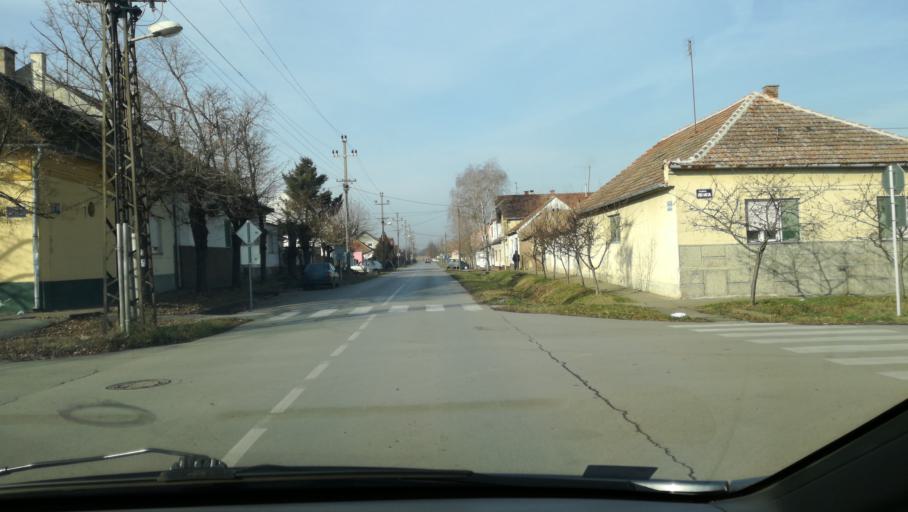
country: RS
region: Autonomna Pokrajina Vojvodina
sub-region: Severnobanatski Okrug
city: Kikinda
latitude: 45.8398
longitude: 20.4728
